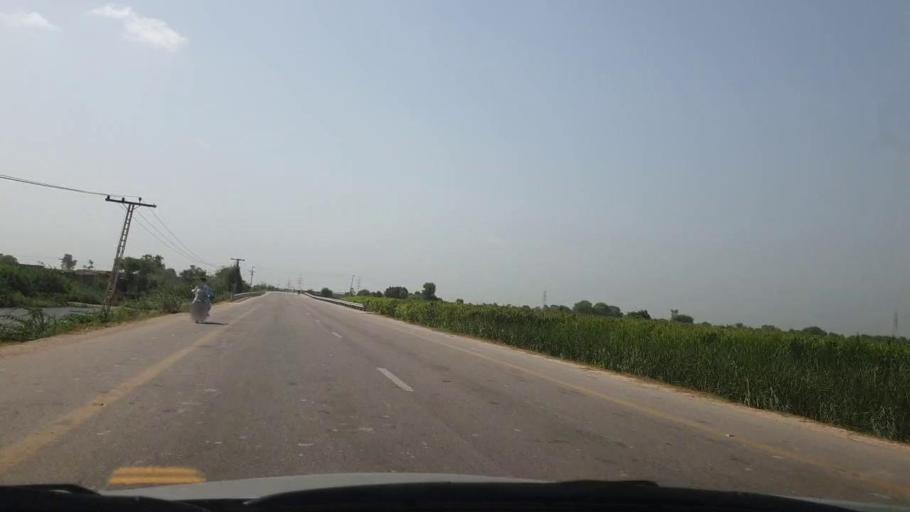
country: PK
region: Sindh
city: Matli
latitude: 25.0537
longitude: 68.6359
